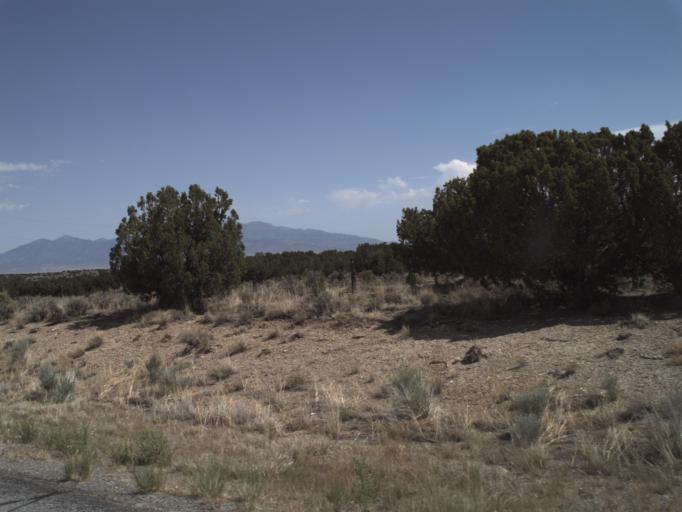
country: US
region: Utah
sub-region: Utah County
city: Eagle Mountain
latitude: 40.0349
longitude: -112.2864
